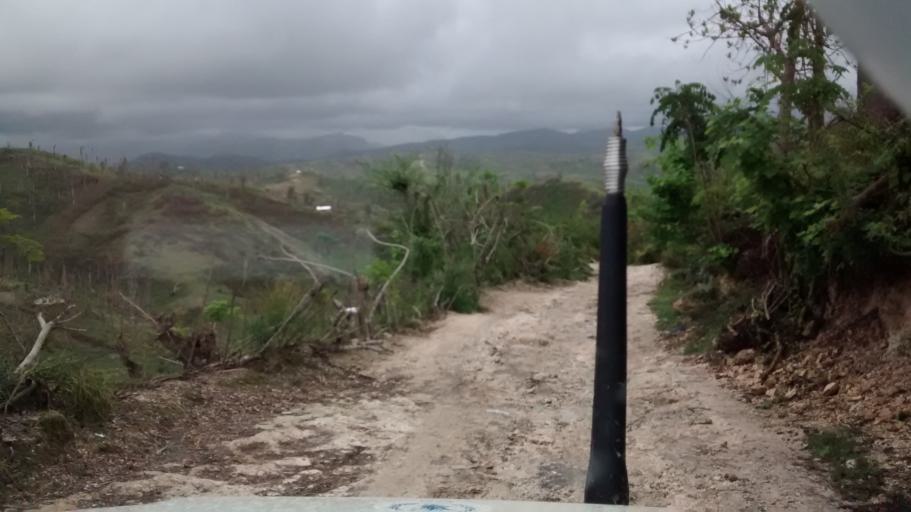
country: HT
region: Grandans
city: Jeremie
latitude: 18.5813
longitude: -74.1495
